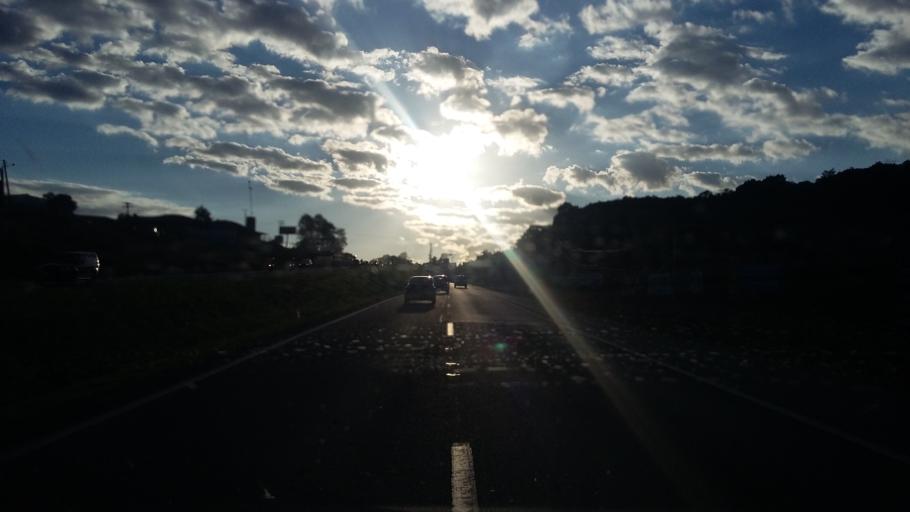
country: BR
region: Parana
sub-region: Campo Largo
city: Campo Largo
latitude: -25.4331
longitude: -49.4171
